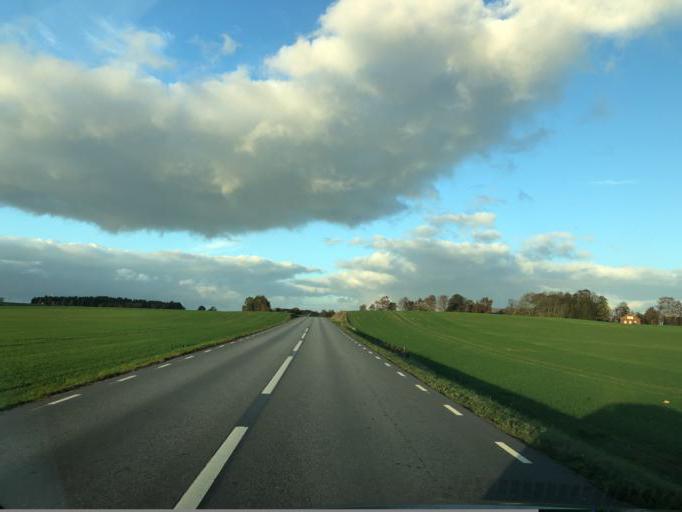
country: SE
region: Skane
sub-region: Svalovs Kommun
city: Teckomatorp
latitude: 55.8482
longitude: 13.1172
